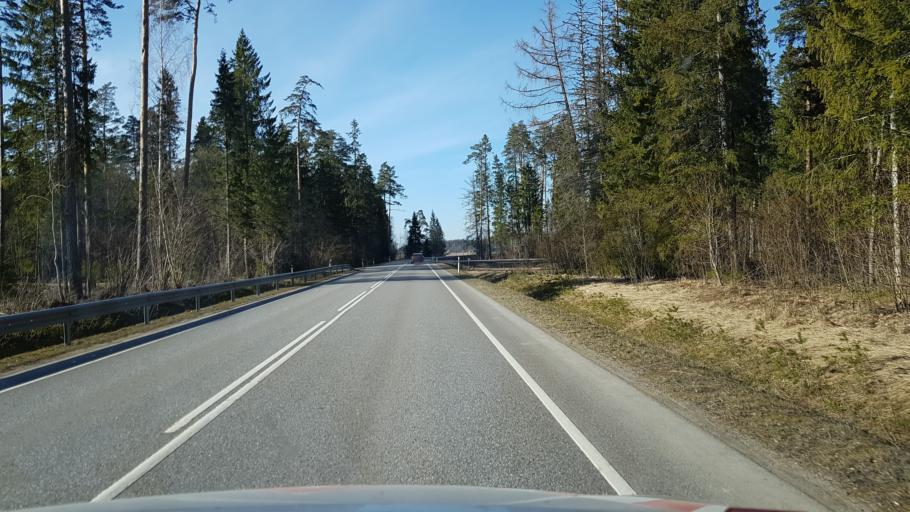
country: EE
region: Laeaene-Virumaa
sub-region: Vinni vald
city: Vinni
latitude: 59.1765
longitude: 26.5787
